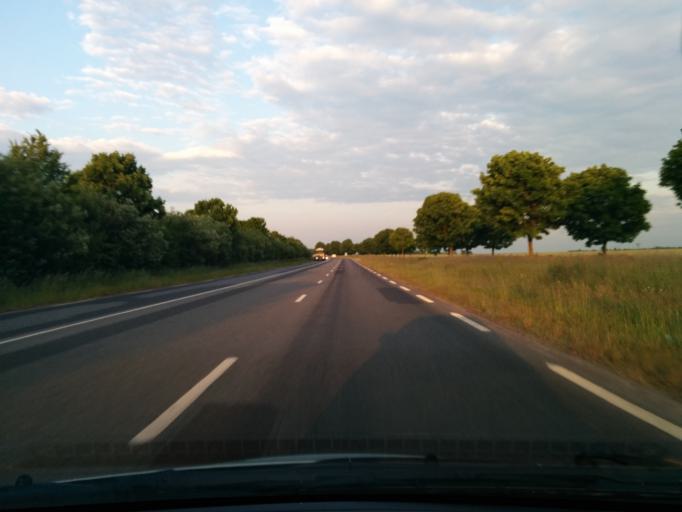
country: FR
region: Haute-Normandie
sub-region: Departement de l'Eure
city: Saint-Marcel
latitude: 49.0722
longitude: 1.4300
